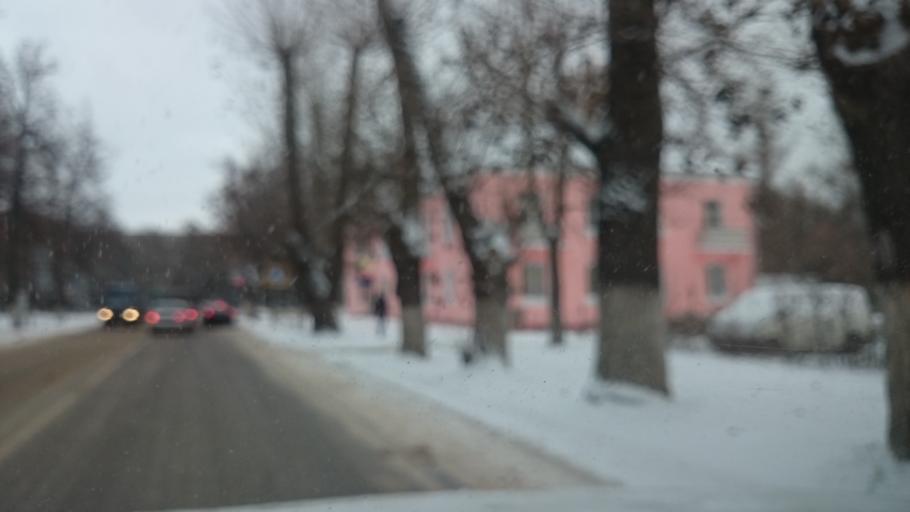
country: RU
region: Tula
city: Mendeleyevskiy
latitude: 54.1715
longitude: 37.5766
